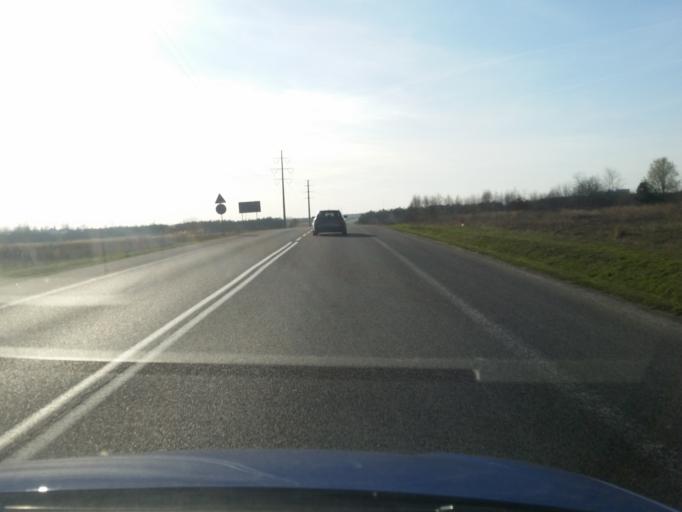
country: PL
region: Lodz Voivodeship
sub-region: Powiat radomszczanski
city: Radomsko
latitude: 51.0824
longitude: 19.4107
